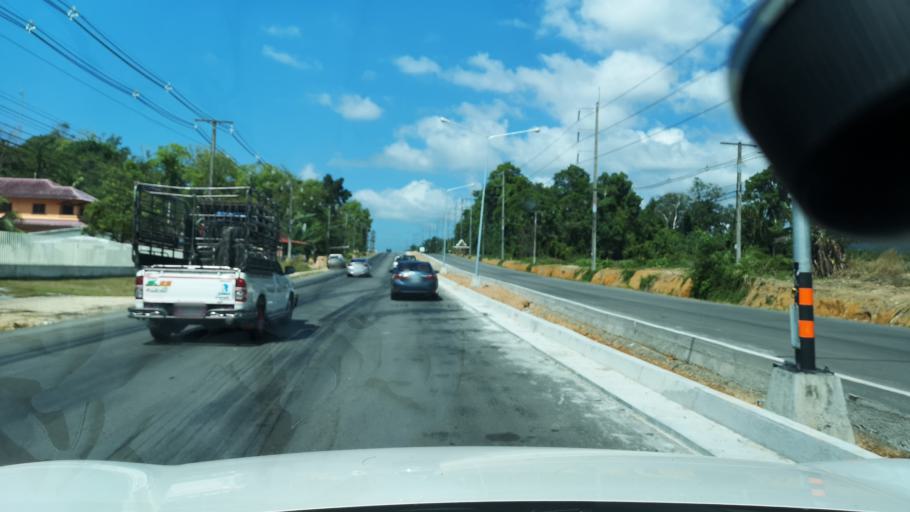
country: TH
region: Phangnga
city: Thai Mueang
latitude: 8.4270
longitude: 98.2584
